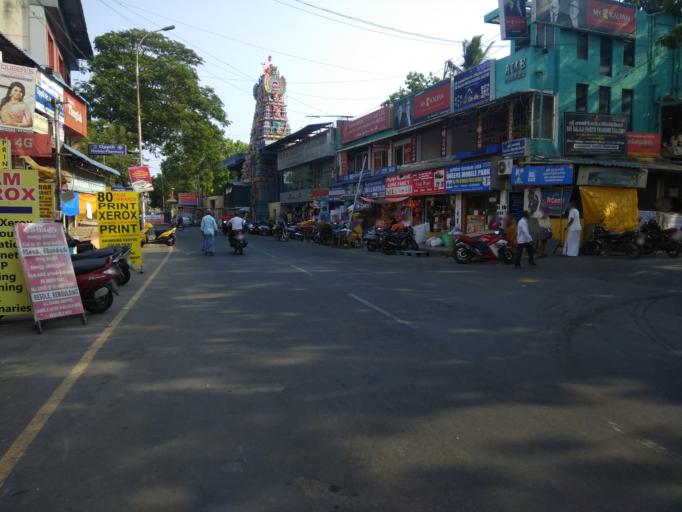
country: IN
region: Tamil Nadu
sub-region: Kancheepuram
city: Saint Thomas Mount
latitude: 12.9855
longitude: 80.1884
